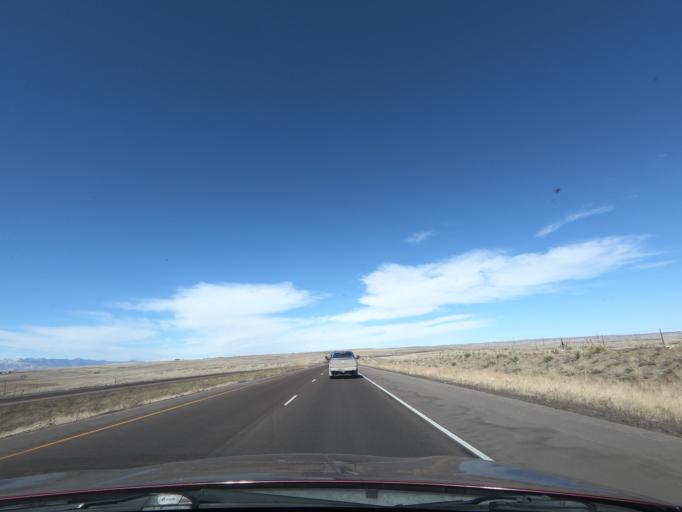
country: US
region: Colorado
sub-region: El Paso County
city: Security-Widefield
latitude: 38.7458
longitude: -104.6827
